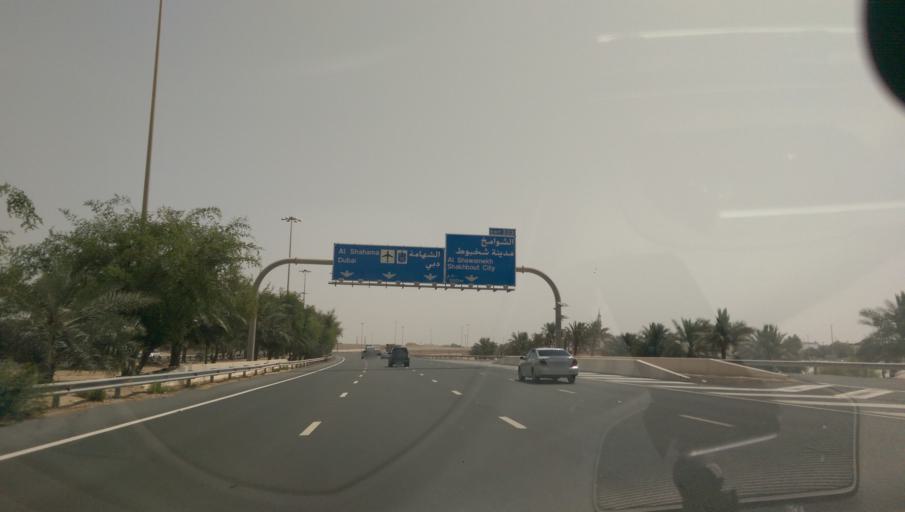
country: AE
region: Abu Dhabi
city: Abu Dhabi
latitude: 24.3338
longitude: 54.6324
